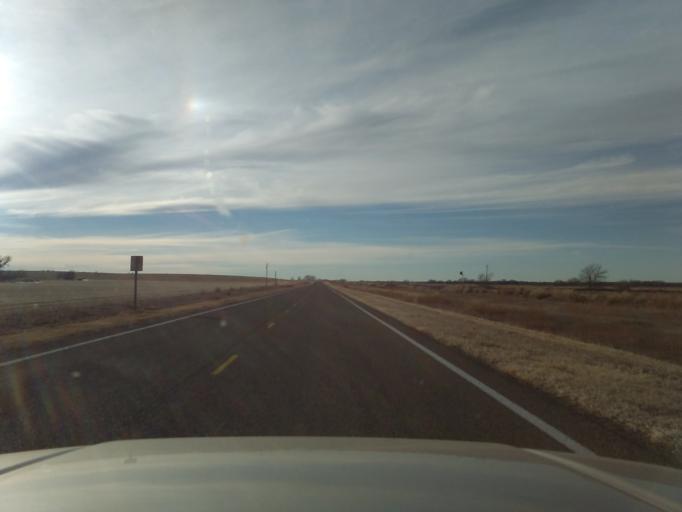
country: US
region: Kansas
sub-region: Norton County
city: Norton
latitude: 39.7537
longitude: -100.1305
